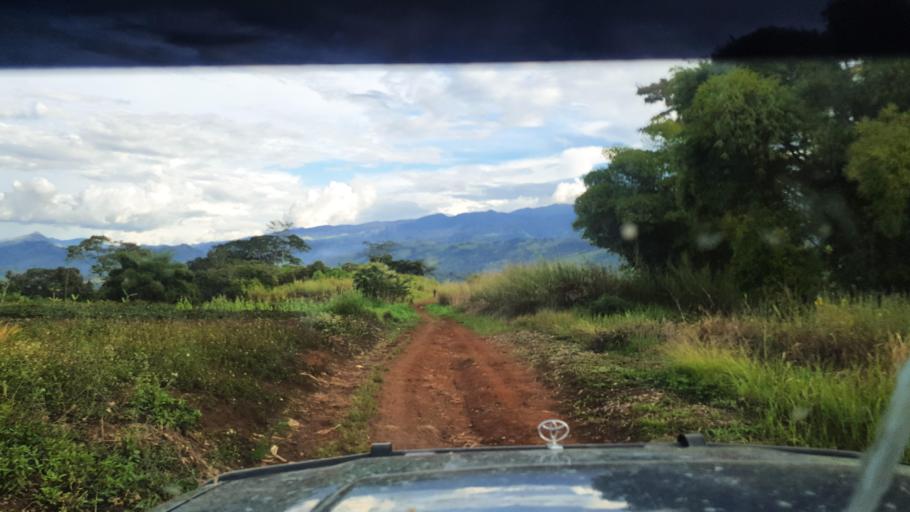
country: PG
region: Jiwaka
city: Minj
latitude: -5.9297
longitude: 144.8196
